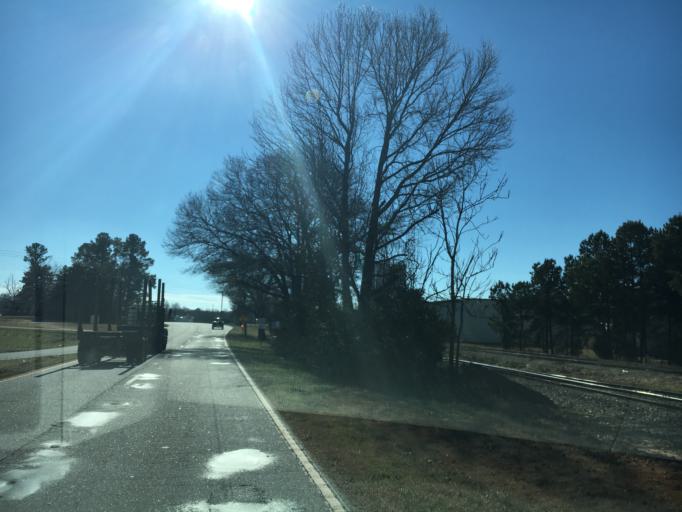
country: US
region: South Carolina
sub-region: Anderson County
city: Homeland Park
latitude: 34.4512
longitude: -82.6689
